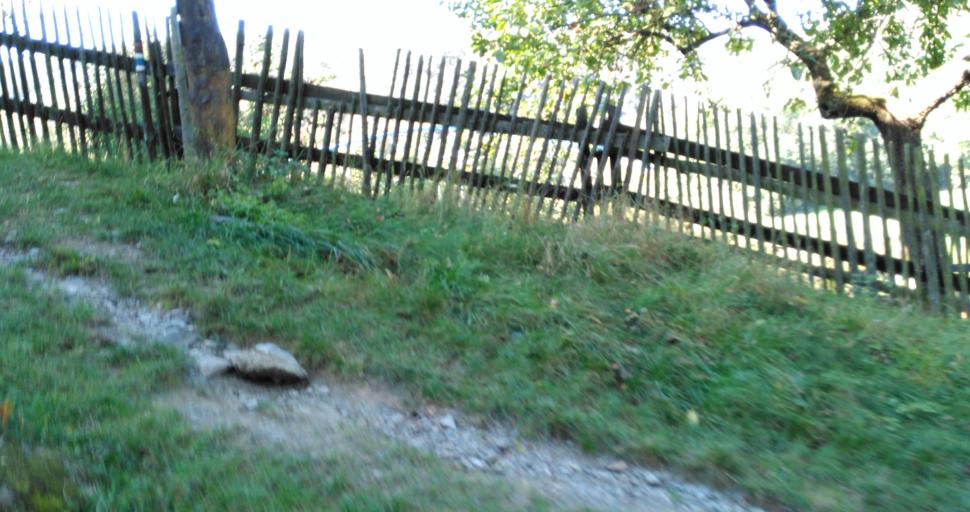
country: CZ
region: Central Bohemia
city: Pavlikov
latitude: 49.9689
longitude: 13.7744
